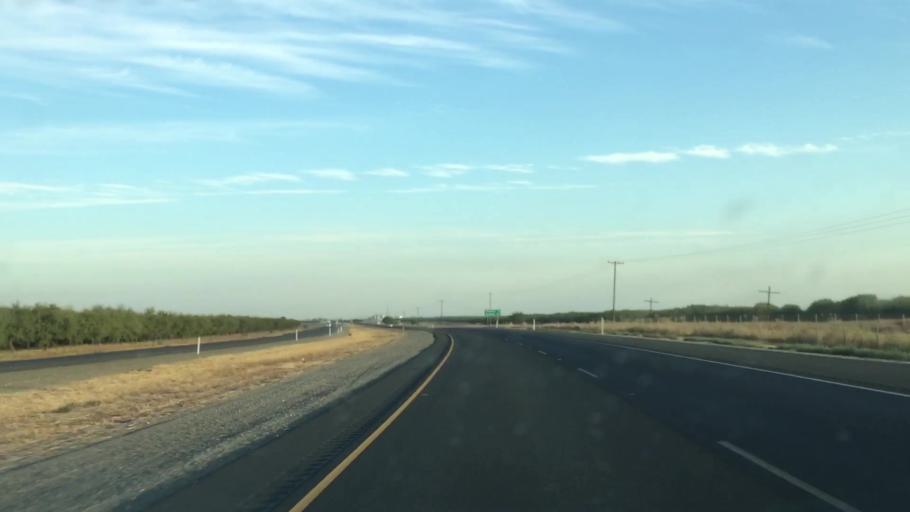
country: US
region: California
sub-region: Yolo County
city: Dunnigan
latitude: 38.9348
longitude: -122.0035
